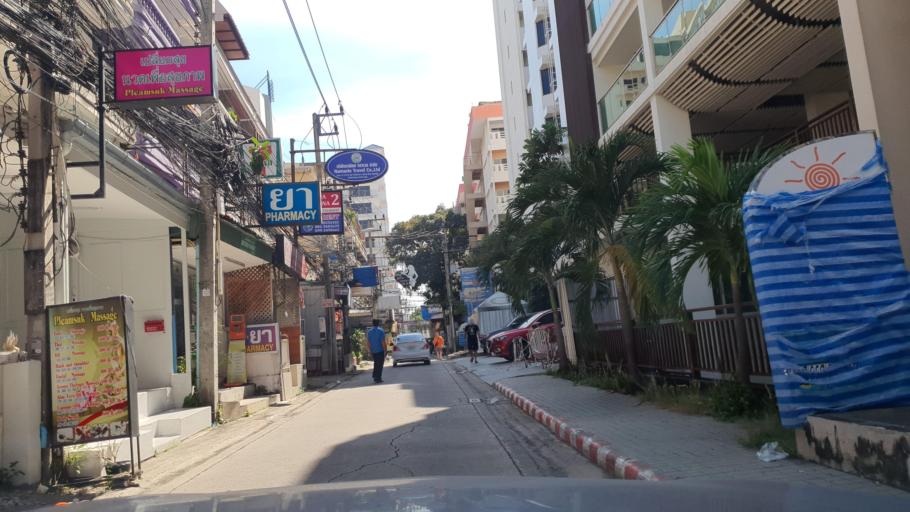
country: TH
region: Chon Buri
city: Phatthaya
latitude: 12.9357
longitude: 100.8842
